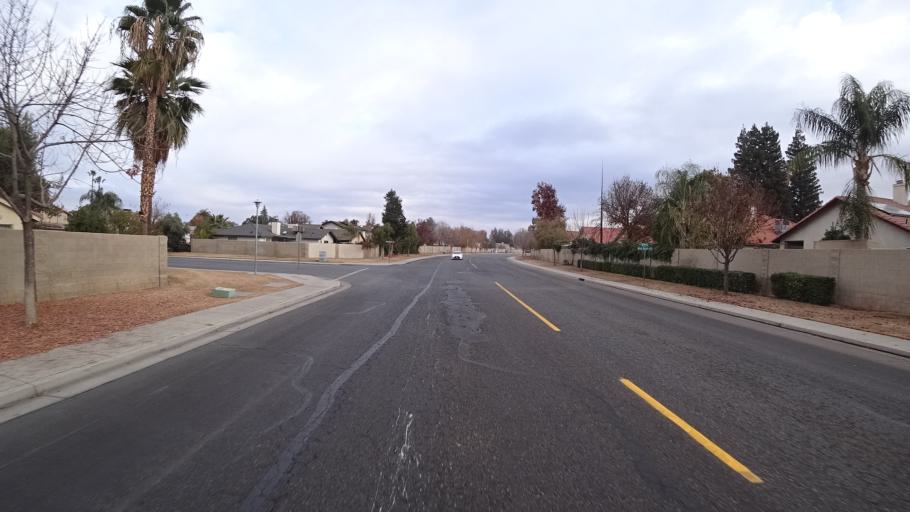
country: US
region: California
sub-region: Kern County
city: Greenacres
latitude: 35.3066
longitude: -119.0883
